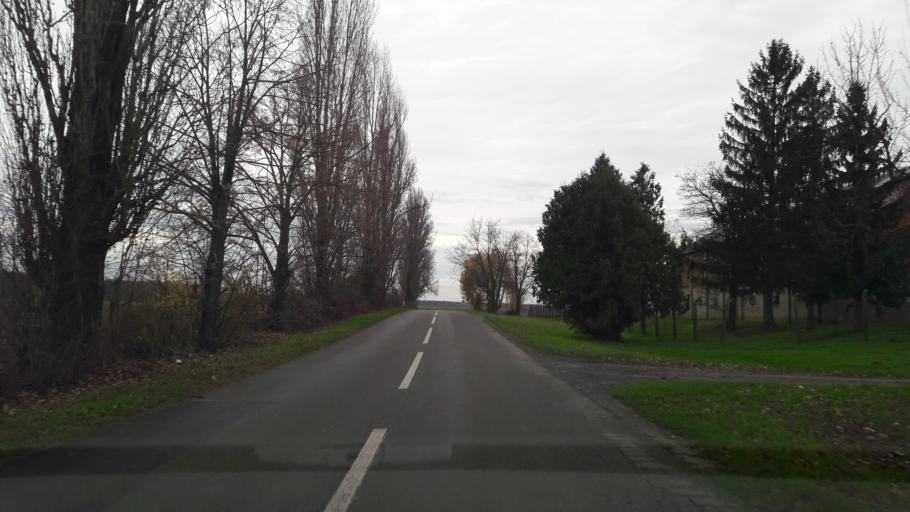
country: HR
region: Virovitick-Podravska
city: Zdenci
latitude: 45.6053
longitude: 18.0000
